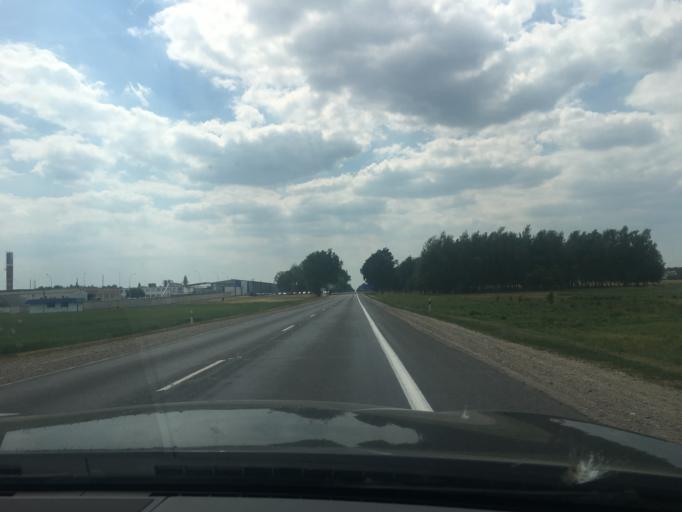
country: BY
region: Brest
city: Pruzhany
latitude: 52.5441
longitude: 24.4548
